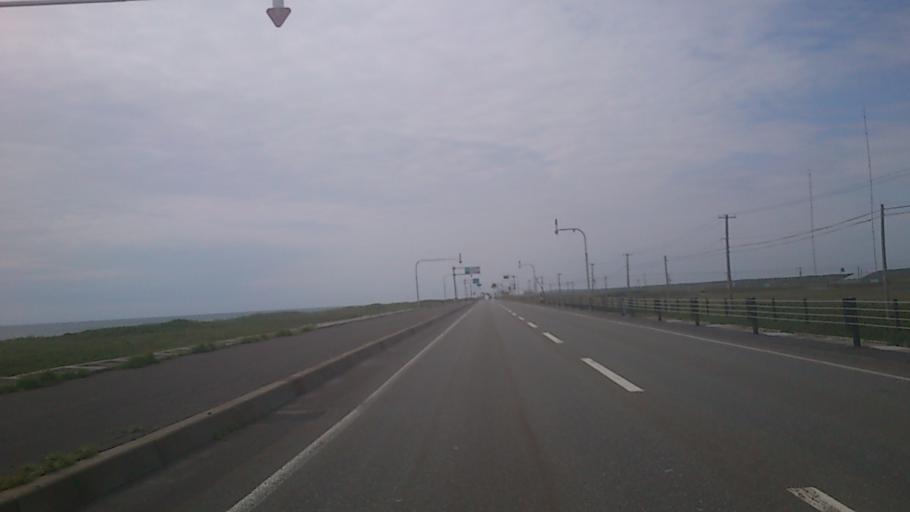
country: JP
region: Hokkaido
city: Makubetsu
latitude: 44.9909
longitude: 141.6877
